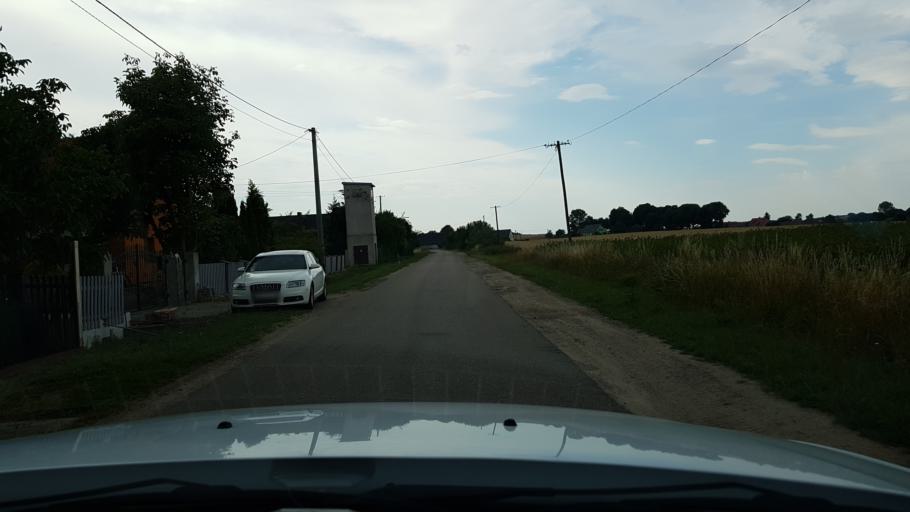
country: PL
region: West Pomeranian Voivodeship
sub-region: Powiat walecki
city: Walcz
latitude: 53.3740
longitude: 16.3255
